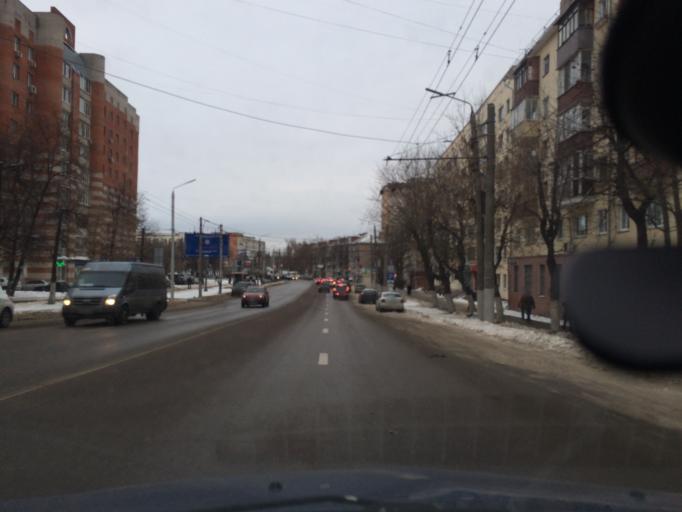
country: RU
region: Tula
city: Tula
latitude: 54.1967
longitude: 37.5849
